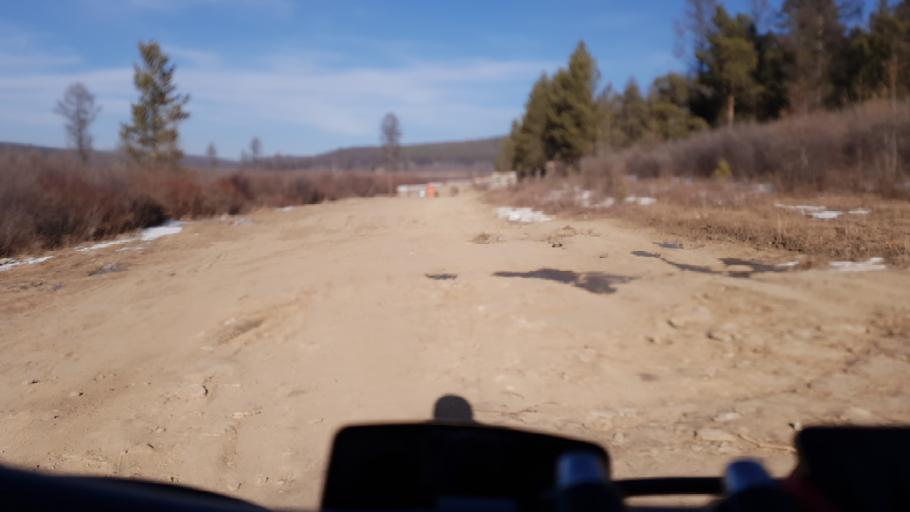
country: MN
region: Ulaanbaatar
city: Ulaanbaatar
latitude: 48.1578
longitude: 106.8815
